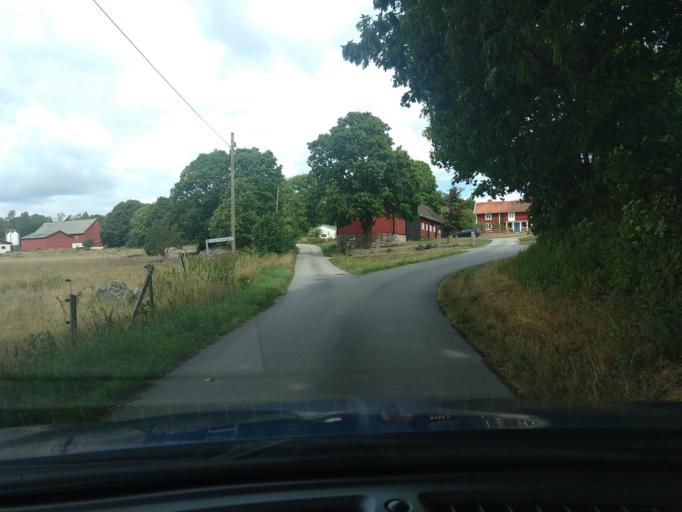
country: SE
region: Blekinge
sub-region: Ronneby Kommun
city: Brakne-Hoby
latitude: 56.2803
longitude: 15.1742
